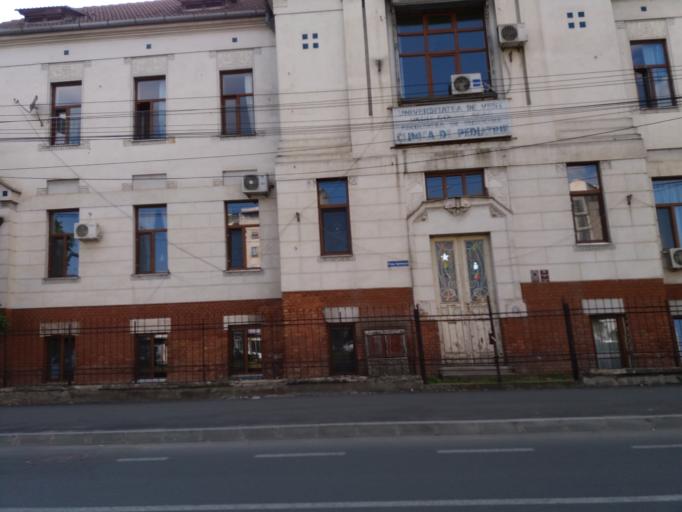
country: RO
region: Arad
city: Arad
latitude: 46.1819
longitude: 21.3097
